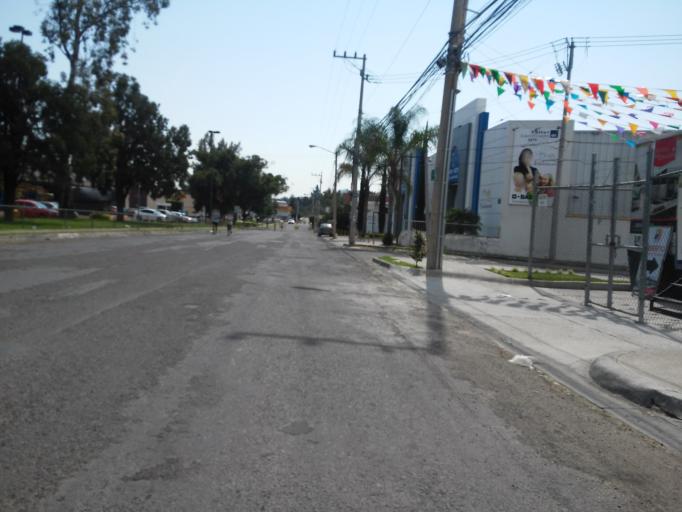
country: MX
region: Jalisco
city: Guadalajara
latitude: 20.6431
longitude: -103.4166
